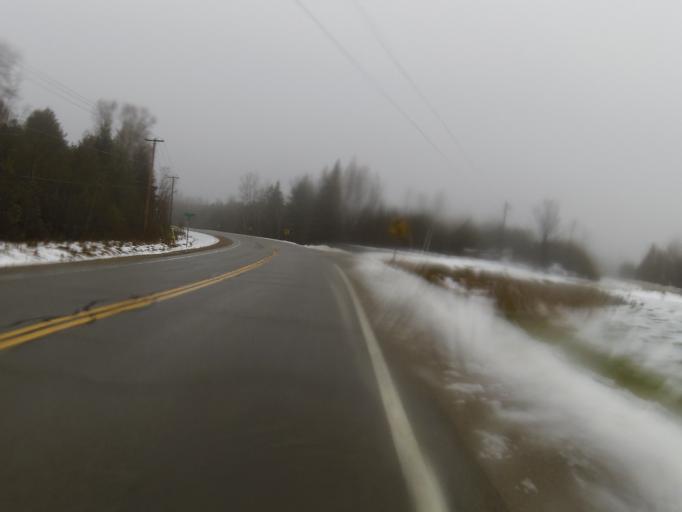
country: CA
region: Ontario
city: Perth
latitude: 44.8192
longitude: -76.3858
